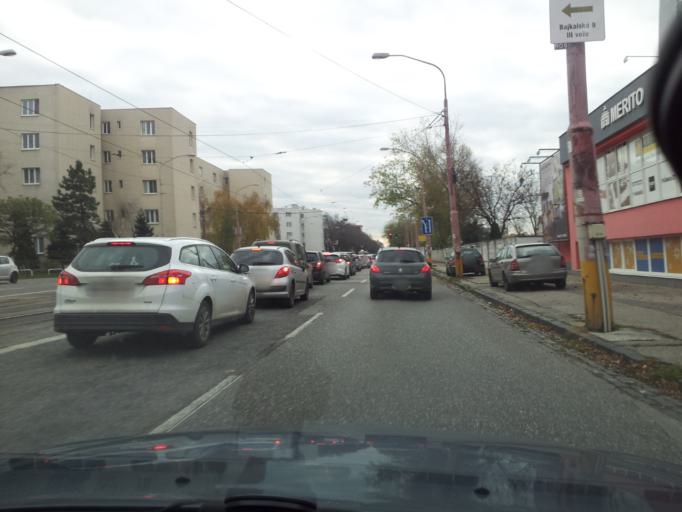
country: SK
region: Bratislavsky
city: Bratislava
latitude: 48.1669
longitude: 17.1364
